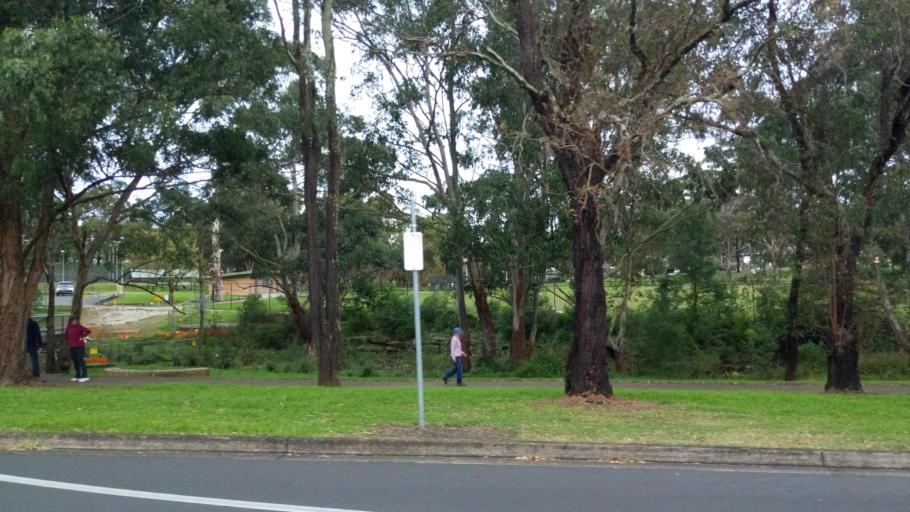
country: AU
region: New South Wales
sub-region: The Hills Shire
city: Baulkham Hills
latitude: -33.7461
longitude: 150.9701
